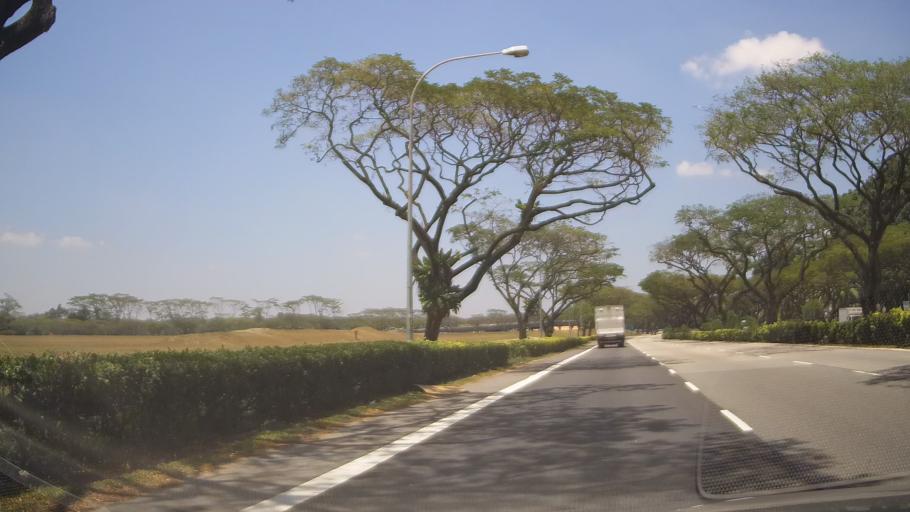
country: MY
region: Johor
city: Johor Bahru
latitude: 1.3527
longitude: 103.7132
